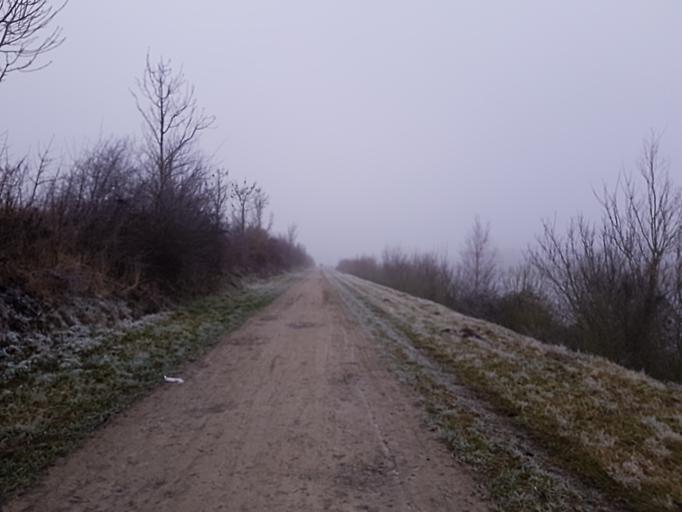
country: BE
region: Flanders
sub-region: Provincie Vlaams-Brabant
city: Grimbergen
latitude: 50.9596
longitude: 4.4037
